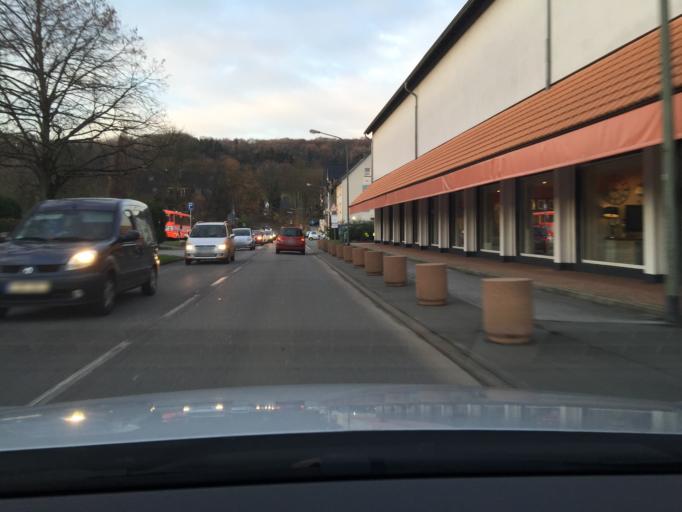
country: DE
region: North Rhine-Westphalia
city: Hattingen
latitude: 51.3736
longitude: 7.1360
